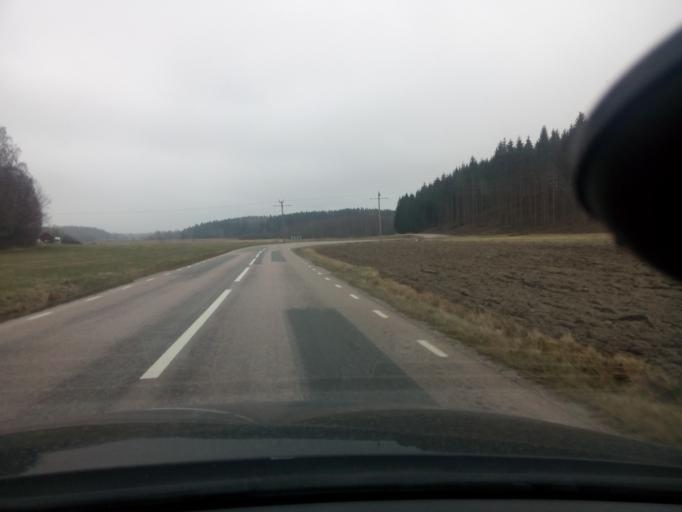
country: SE
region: Soedermanland
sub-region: Gnesta Kommun
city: Gnesta
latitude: 59.0465
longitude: 17.1563
